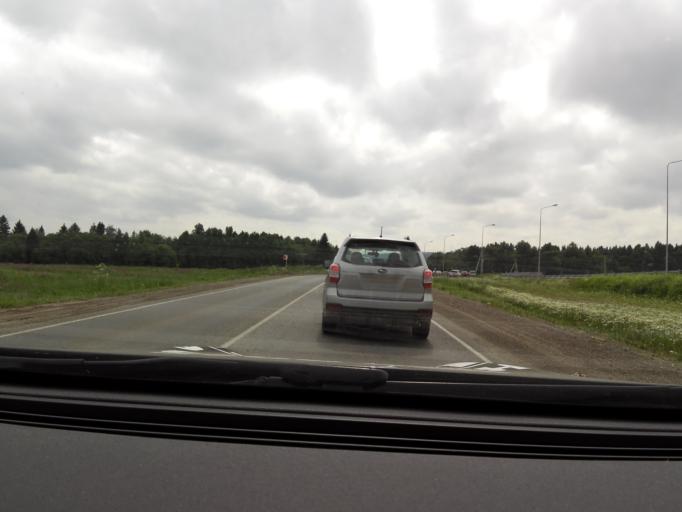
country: RU
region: Perm
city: Zvezdnyy
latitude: 57.7810
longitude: 56.3447
